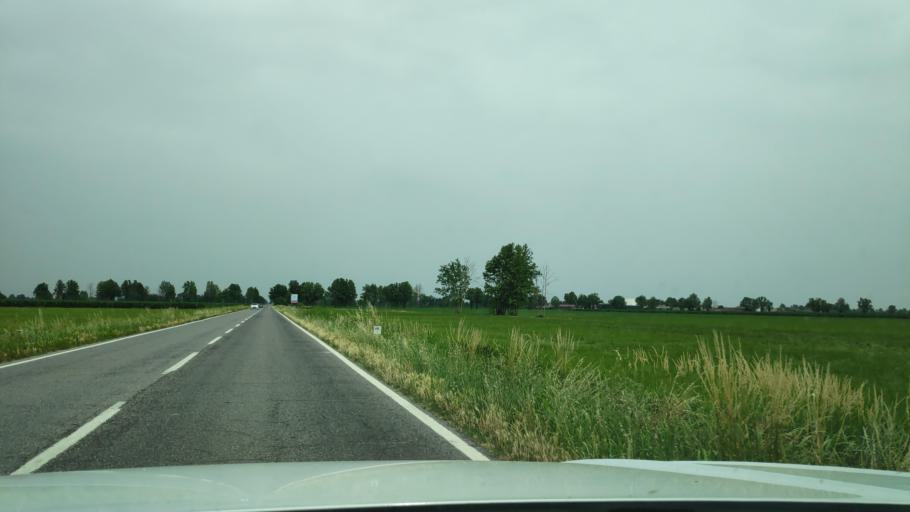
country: IT
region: Lombardy
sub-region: Provincia di Cremona
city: Cremosano
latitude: 45.4064
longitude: 9.6512
